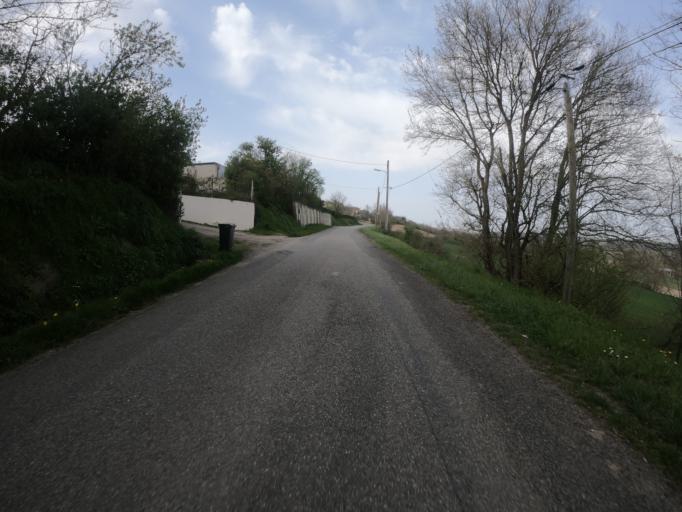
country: FR
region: Midi-Pyrenees
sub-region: Departement de l'Ariege
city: La Tour-du-Crieu
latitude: 43.1385
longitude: 1.7125
